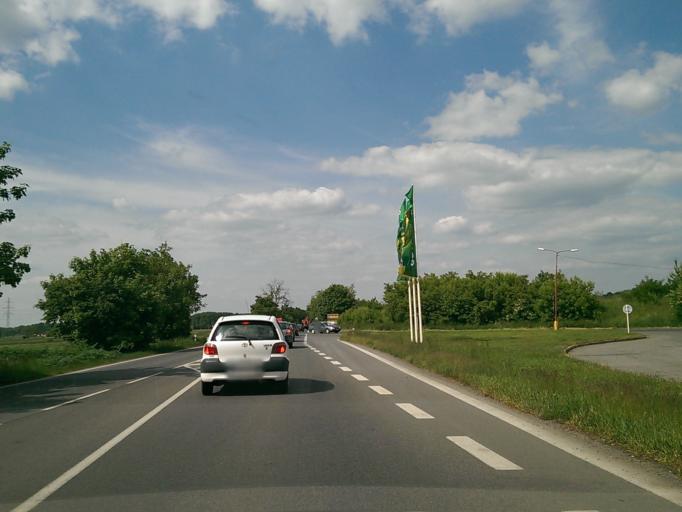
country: CZ
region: Central Bohemia
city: Libis
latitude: 50.2817
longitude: 14.4958
